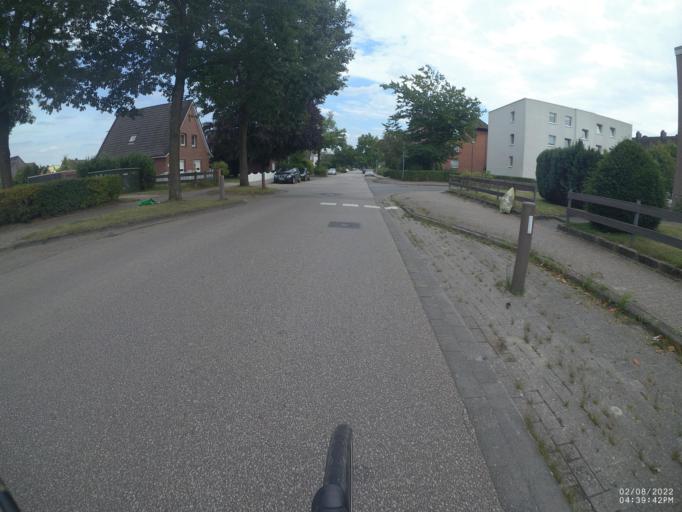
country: DE
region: Lower Saxony
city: Oldenburg
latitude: 53.1659
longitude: 8.1938
